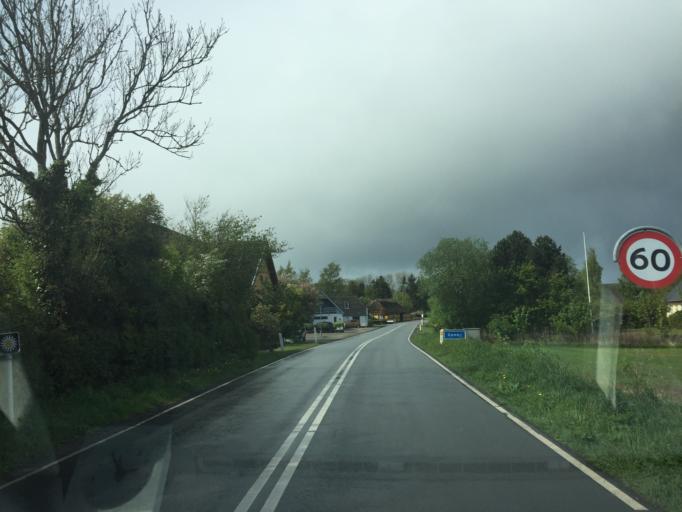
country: DK
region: South Denmark
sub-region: Nordfyns Kommune
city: Bogense
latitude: 55.4728
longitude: 10.0856
